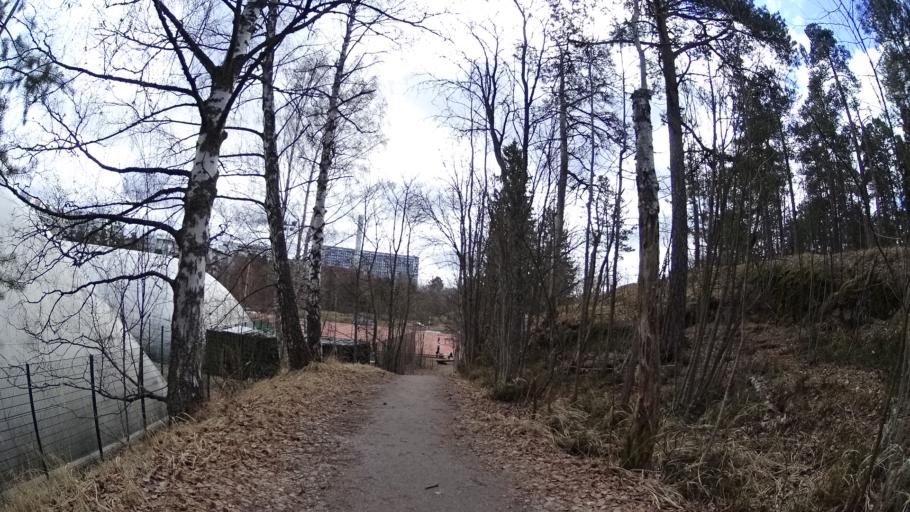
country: FI
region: Uusimaa
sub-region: Helsinki
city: Helsinki
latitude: 60.1893
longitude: 24.8969
